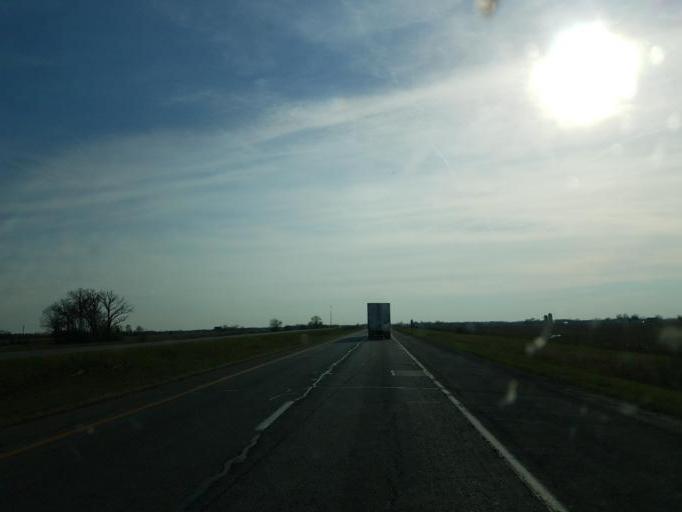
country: US
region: Ohio
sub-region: Madison County
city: Mount Sterling
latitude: 39.7804
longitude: -83.2588
